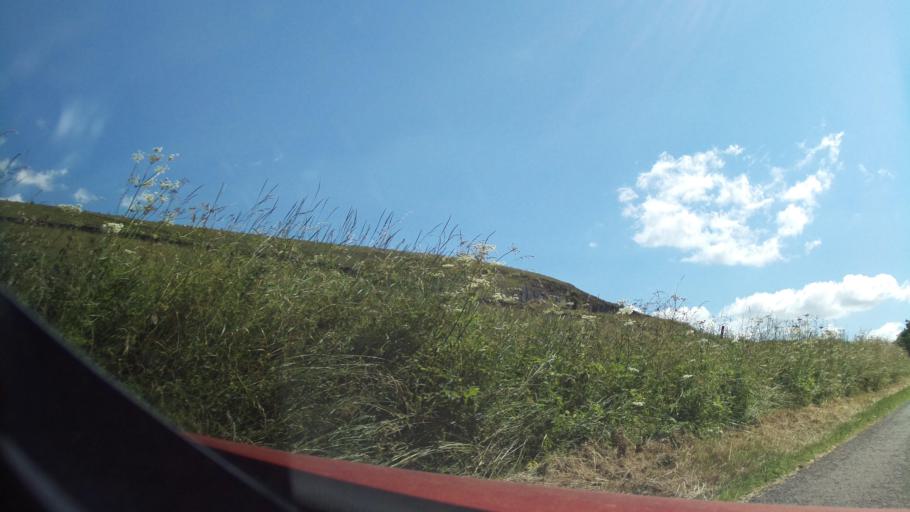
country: GB
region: England
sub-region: Derbyshire
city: Buxton
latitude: 53.2775
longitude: -1.8446
